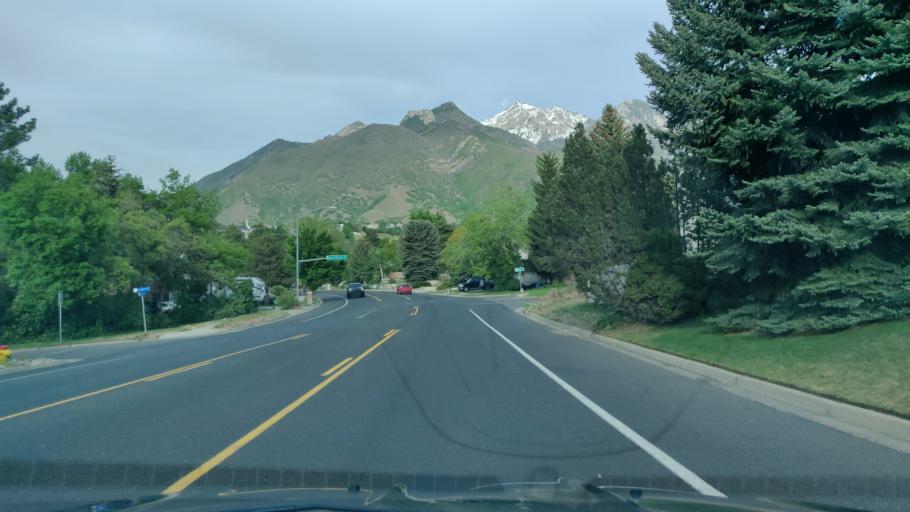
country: US
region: Utah
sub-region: Salt Lake County
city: Little Cottonwood Creek Valley
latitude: 40.6022
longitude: -111.8194
